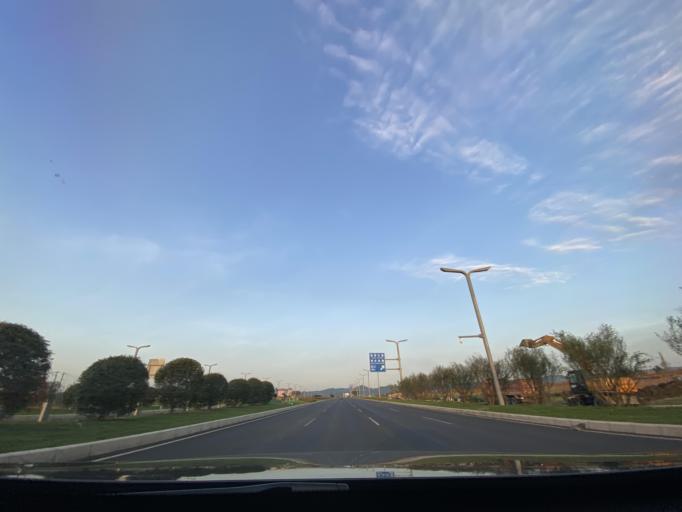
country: CN
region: Sichuan
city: Longquan
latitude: 30.5999
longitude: 104.2634
